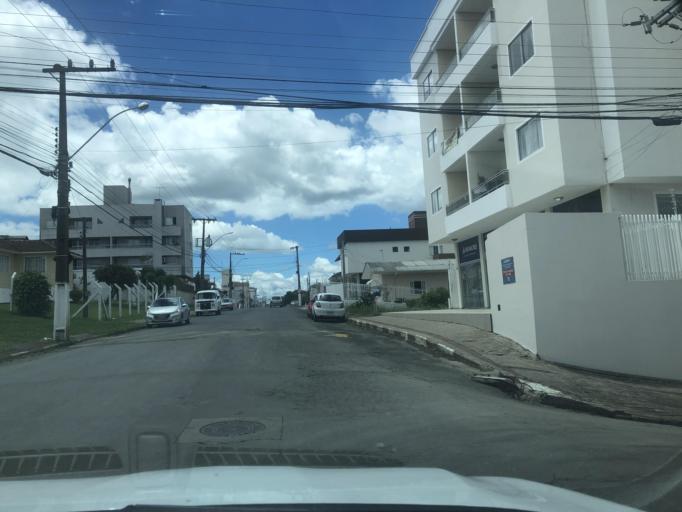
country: BR
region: Santa Catarina
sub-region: Lages
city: Lages
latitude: -27.8058
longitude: -50.3019
